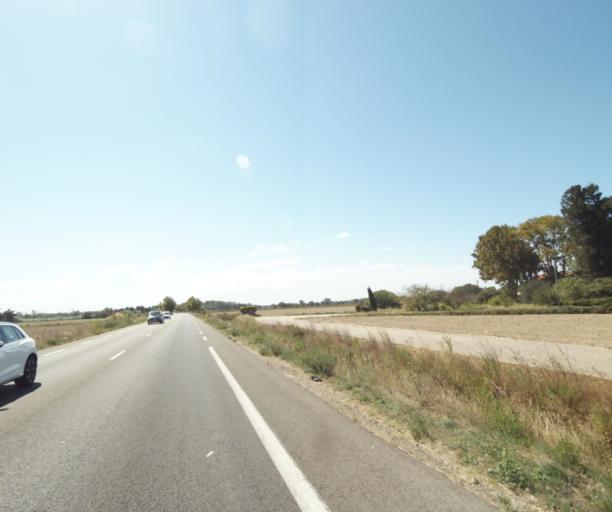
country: FR
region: Languedoc-Roussillon
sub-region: Departement du Gard
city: Rodilhan
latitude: 43.8312
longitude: 4.4238
